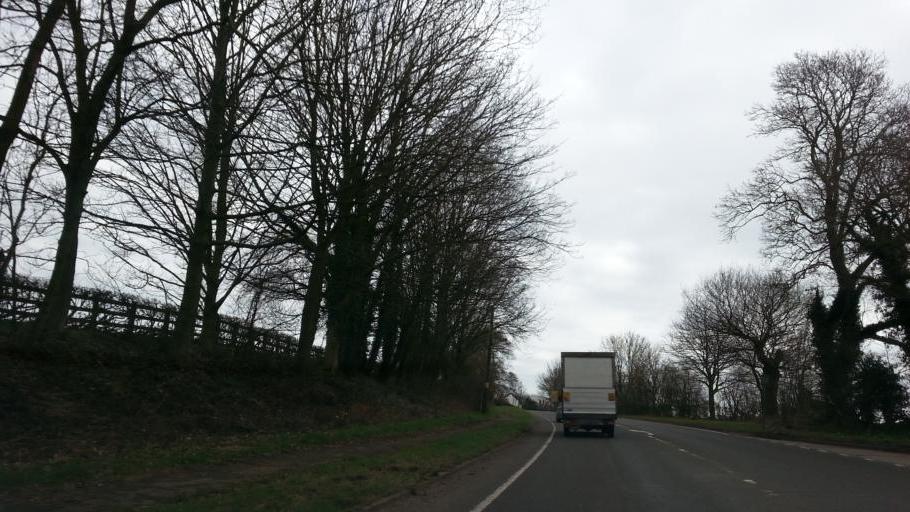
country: GB
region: England
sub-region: Staffordshire
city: Stafford
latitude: 52.8677
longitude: -2.0858
